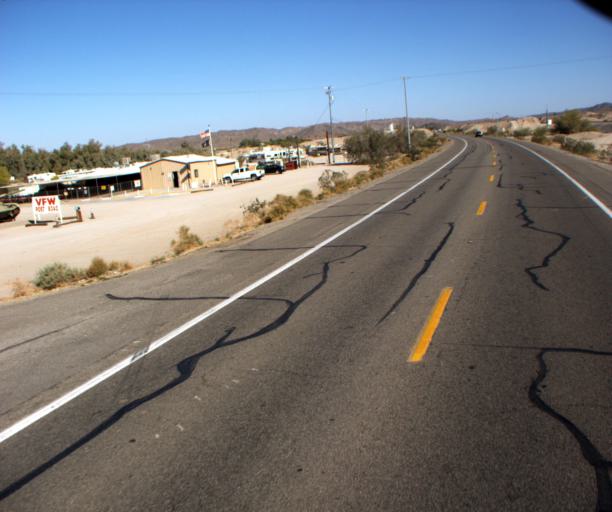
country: US
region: Arizona
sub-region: Yuma County
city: Fortuna Foothills
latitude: 32.7275
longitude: -114.4214
